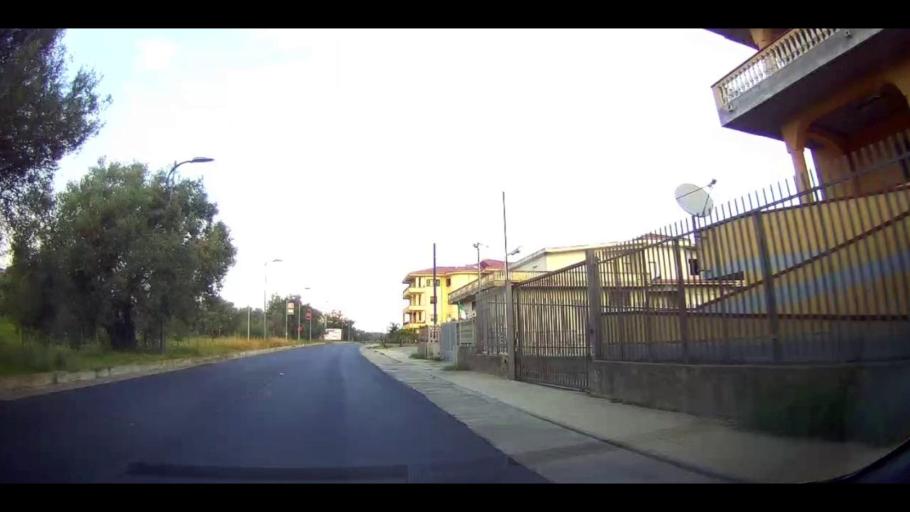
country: IT
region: Calabria
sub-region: Provincia di Crotone
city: Torretta
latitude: 39.4597
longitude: 17.0299
